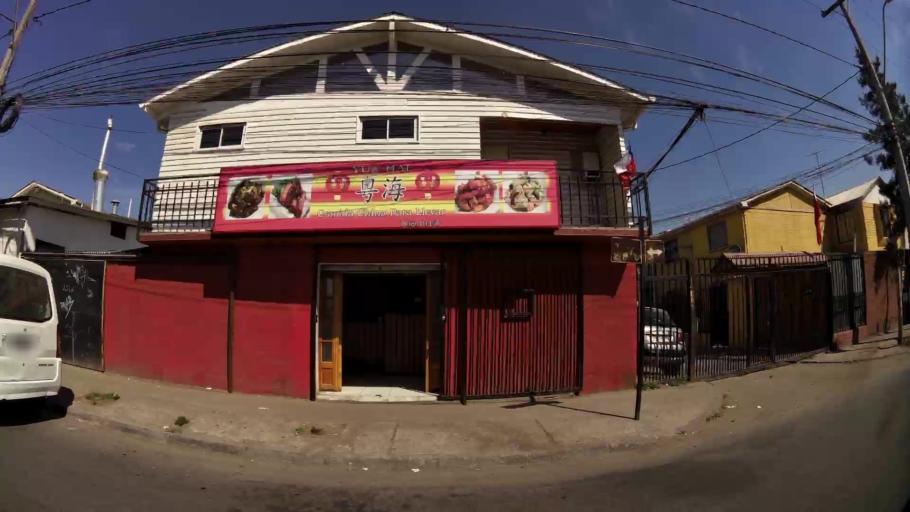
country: CL
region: Santiago Metropolitan
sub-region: Provincia de Cordillera
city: Puente Alto
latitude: -33.6294
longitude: -70.6147
